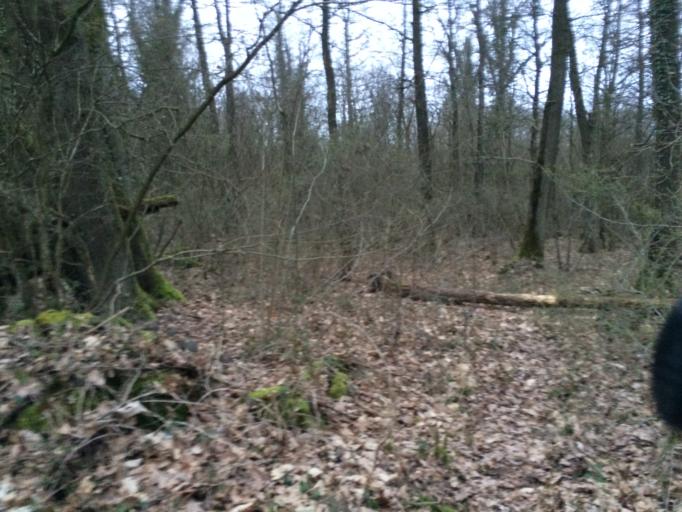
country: FR
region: Ile-de-France
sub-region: Departement de l'Essonne
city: Igny
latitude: 48.7422
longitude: 2.2119
